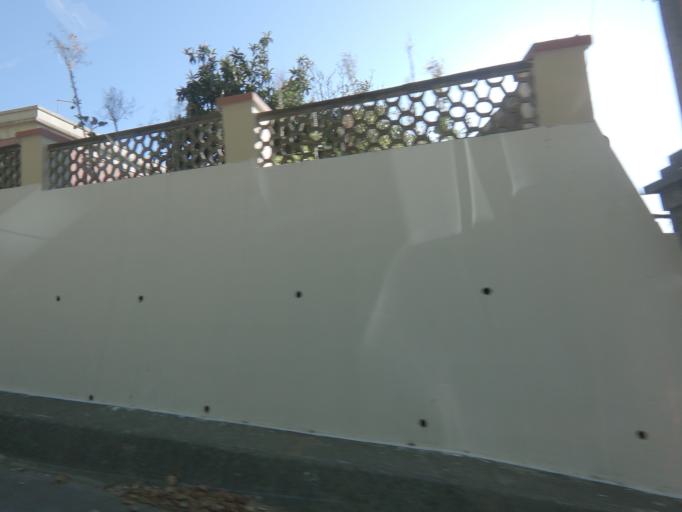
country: PT
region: Setubal
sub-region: Palmela
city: Palmela
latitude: 38.5741
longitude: -8.9061
